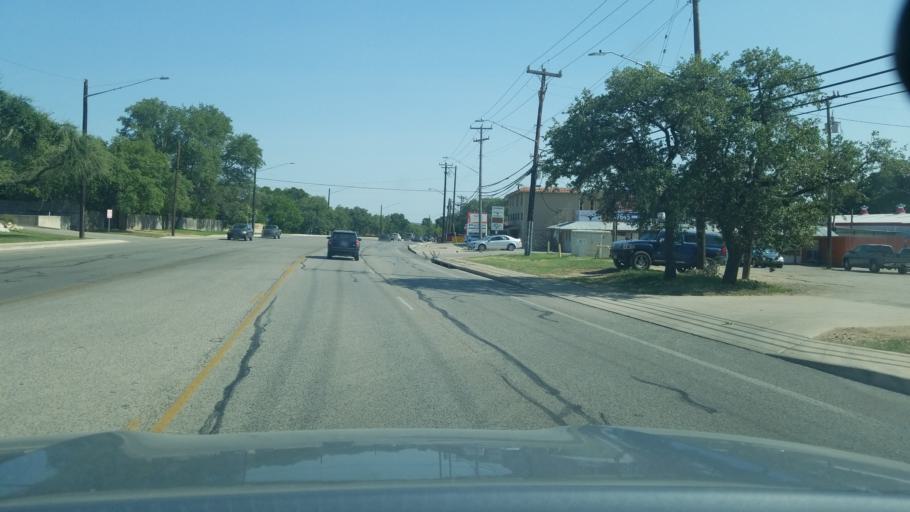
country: US
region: Texas
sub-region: Bexar County
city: Hollywood Park
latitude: 29.6033
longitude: -98.5082
